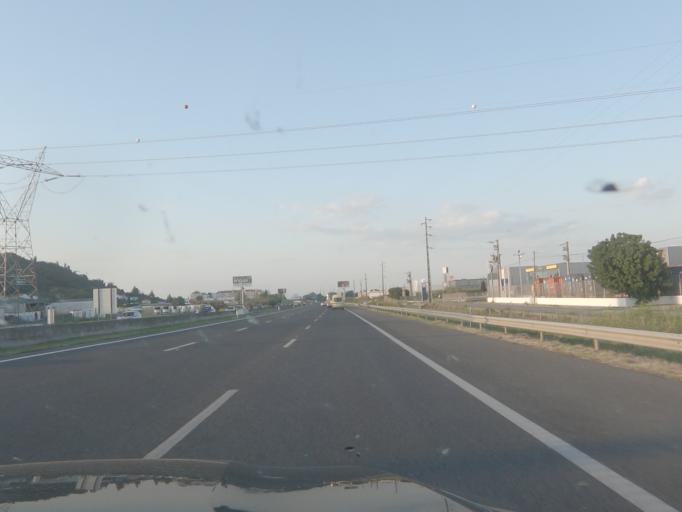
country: PT
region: Lisbon
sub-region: Vila Franca de Xira
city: Castanheira do Ribatejo
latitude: 38.9790
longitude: -8.9751
